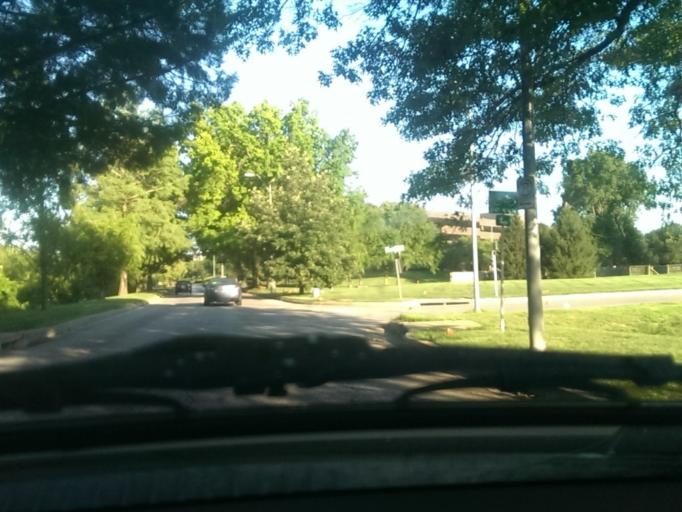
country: US
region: Kansas
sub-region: Johnson County
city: Leawood
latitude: 38.9610
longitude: -94.6017
